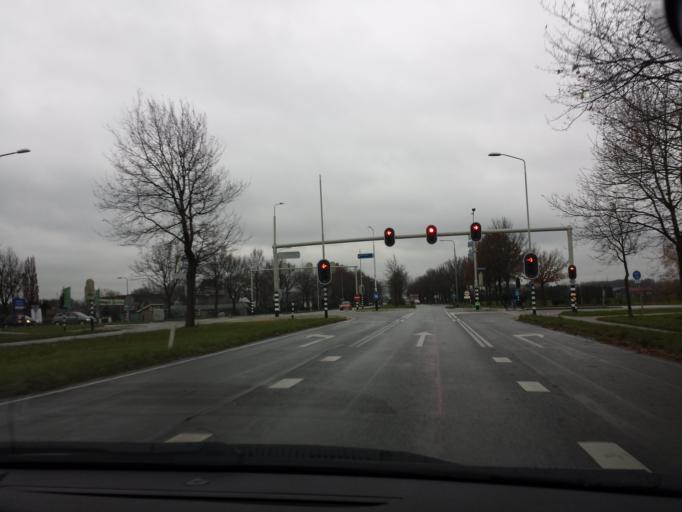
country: NL
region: Limburg
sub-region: Gemeente Sittard-Geleen
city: Limbricht
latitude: 51.0362
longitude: 5.8487
